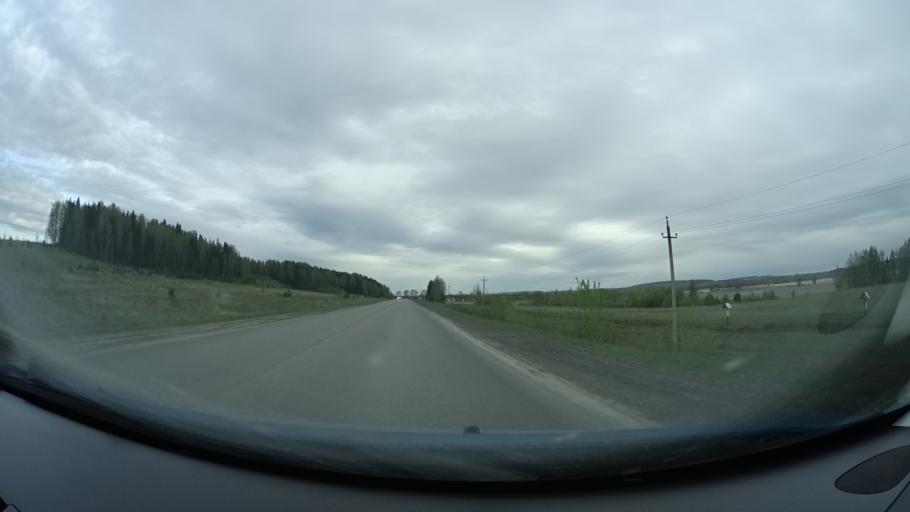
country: RU
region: Perm
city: Osa
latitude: 57.2130
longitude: 55.5908
